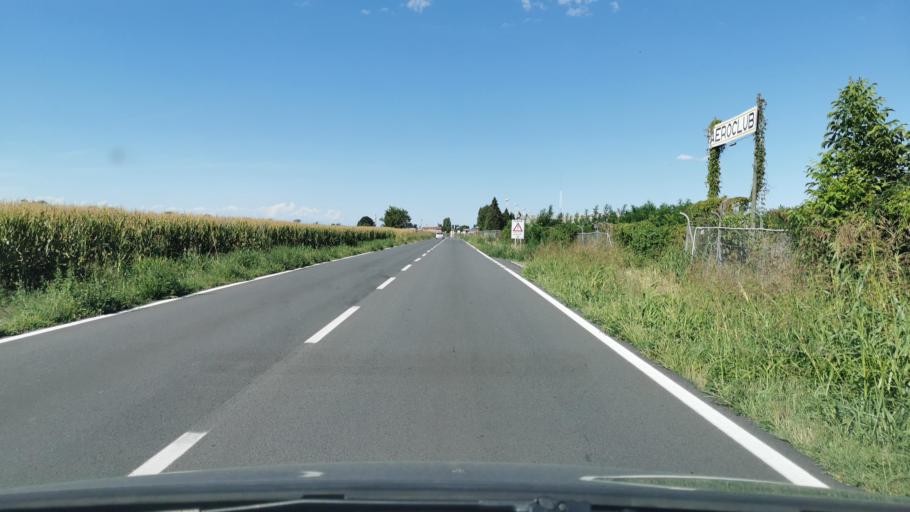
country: IT
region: Piedmont
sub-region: Provincia di Cuneo
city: Vottignasco
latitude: 44.5425
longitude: 7.6139
